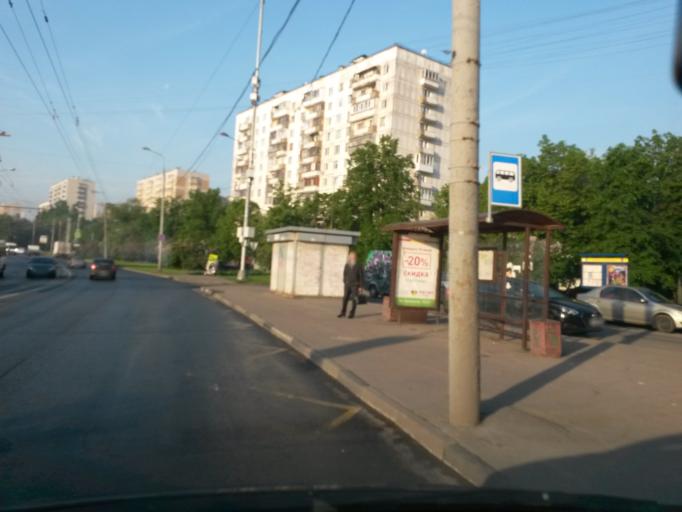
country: RU
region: Moscow
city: Gol'yanovo
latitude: 55.8212
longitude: 37.7983
